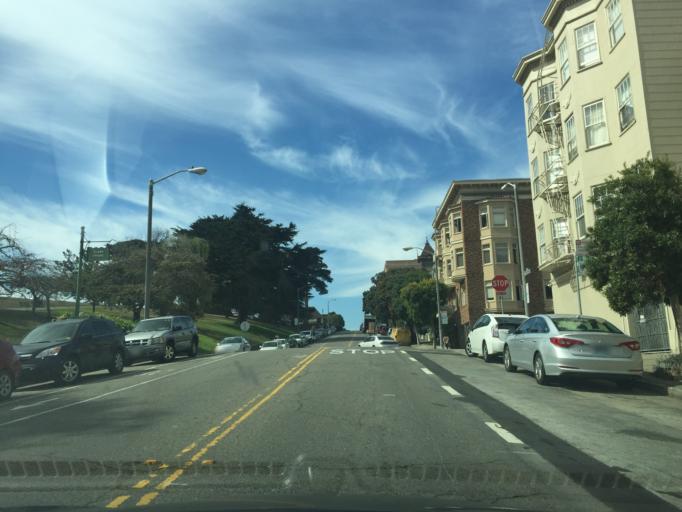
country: US
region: California
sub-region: San Francisco County
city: San Francisco
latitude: 37.7774
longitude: -122.4344
